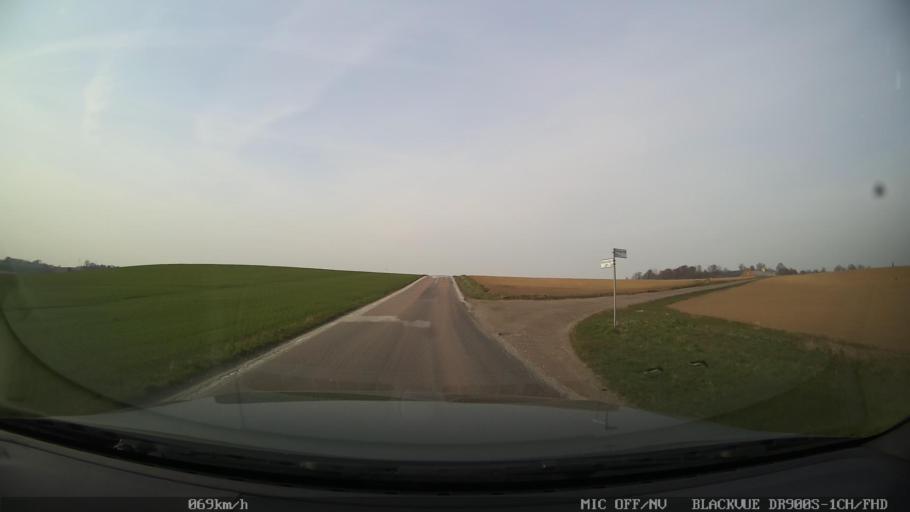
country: SE
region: Skane
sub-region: Ystads Kommun
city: Ystad
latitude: 55.4485
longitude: 13.8318
